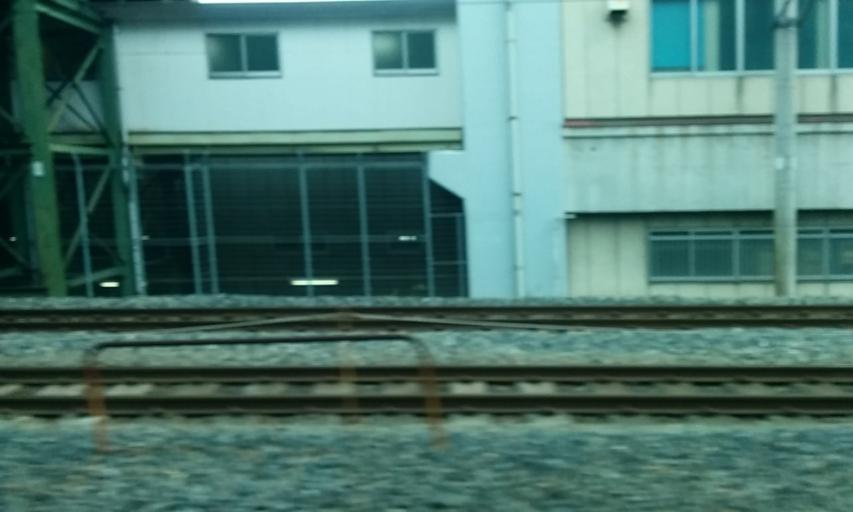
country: JP
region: Saitama
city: Kawaguchi
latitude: 35.7465
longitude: 139.7474
